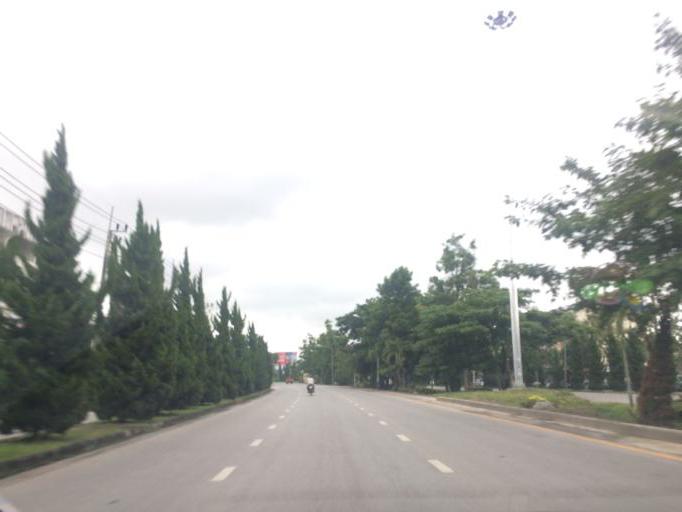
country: TH
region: Chiang Rai
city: Chiang Rai
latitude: 19.9053
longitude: 99.8408
